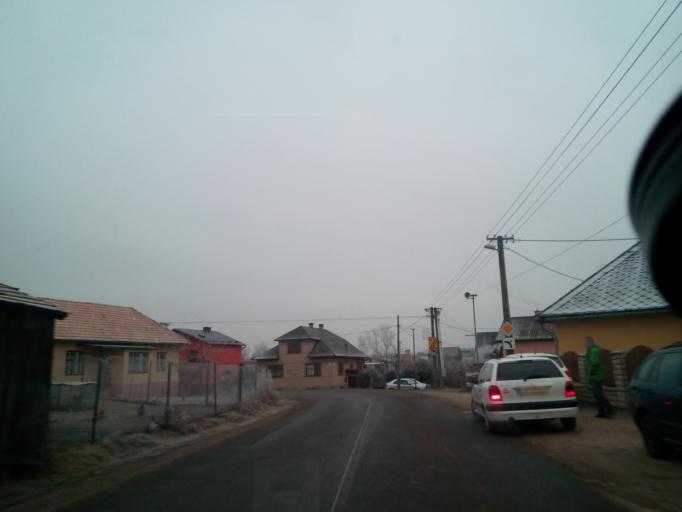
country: SK
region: Presovsky
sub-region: Okres Poprad
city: Poprad
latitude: 48.9735
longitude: 20.4066
